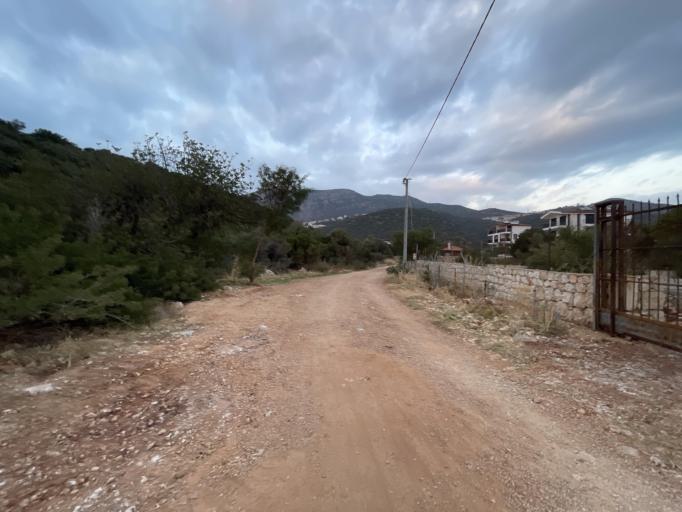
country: TR
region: Antalya
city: Kas
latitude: 36.1866
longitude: 29.6524
